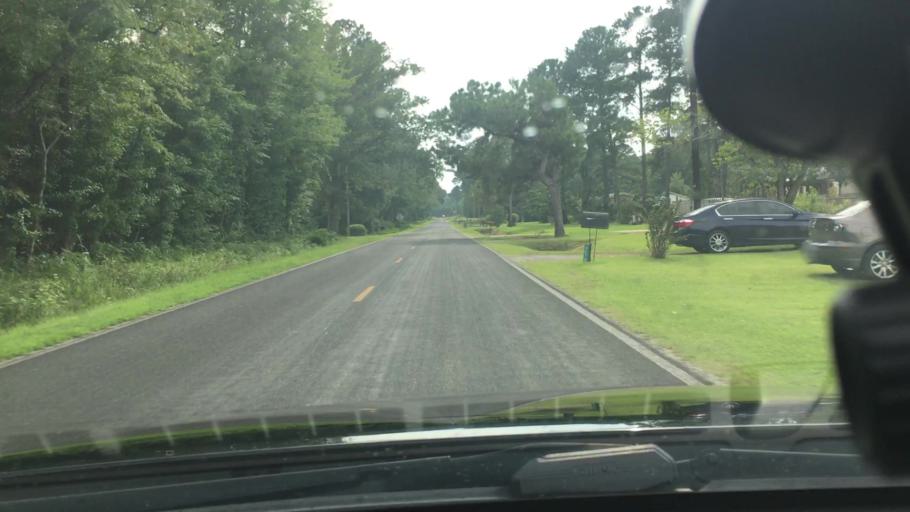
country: US
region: North Carolina
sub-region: Craven County
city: Vanceboro
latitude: 35.3357
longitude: -77.1635
